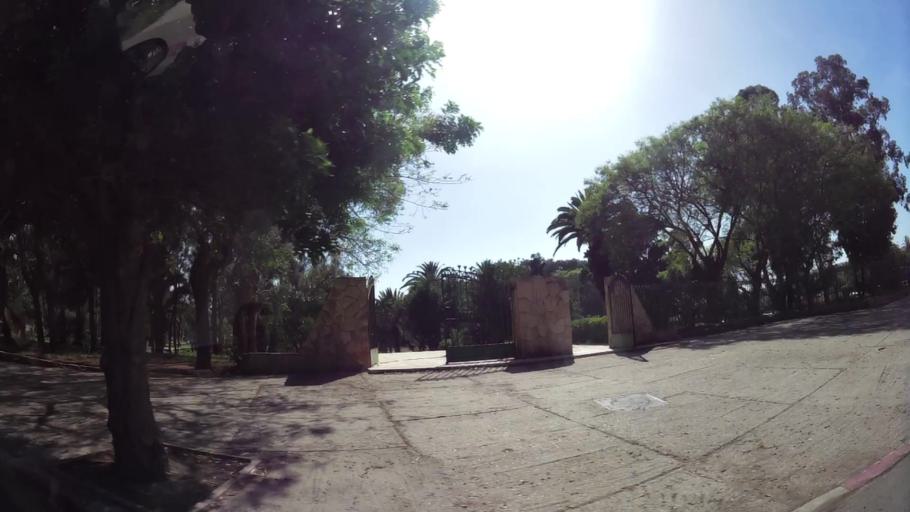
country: MA
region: Souss-Massa-Draa
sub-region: Agadir-Ida-ou-Tnan
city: Agadir
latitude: 30.4201
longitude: -9.5918
